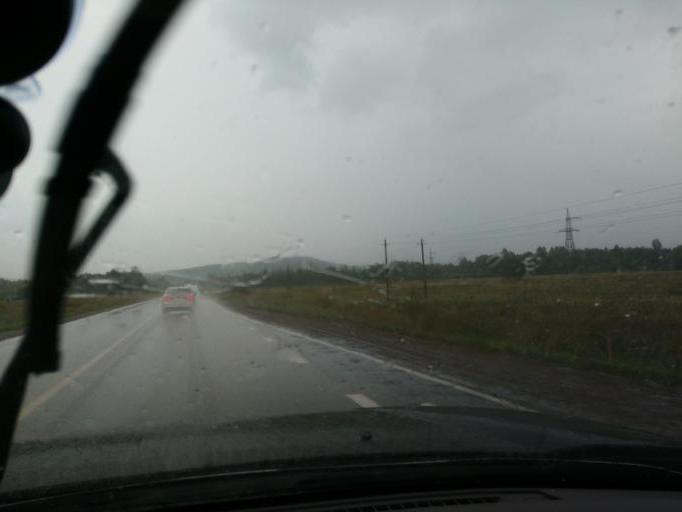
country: RU
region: Perm
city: Osa
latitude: 57.1803
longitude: 55.5605
